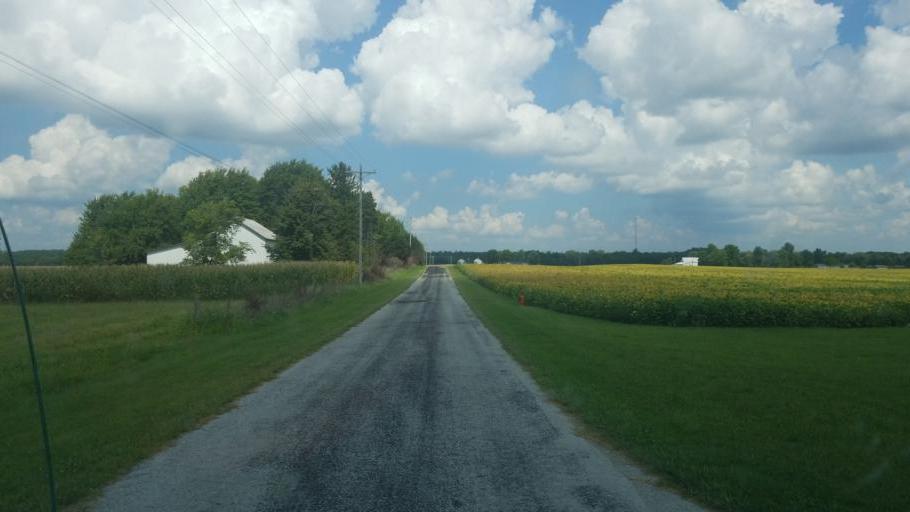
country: US
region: Ohio
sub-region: Hardin County
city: Kenton
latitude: 40.6985
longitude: -83.6386
